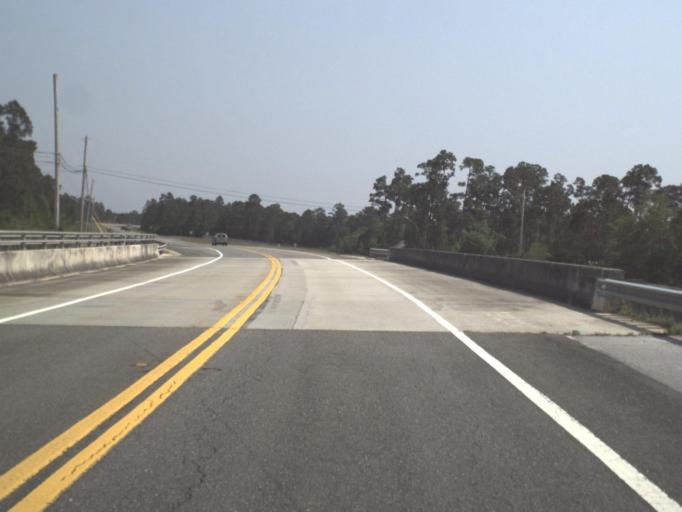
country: US
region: Florida
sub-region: Santa Rosa County
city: Bagdad
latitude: 30.5145
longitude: -87.0869
